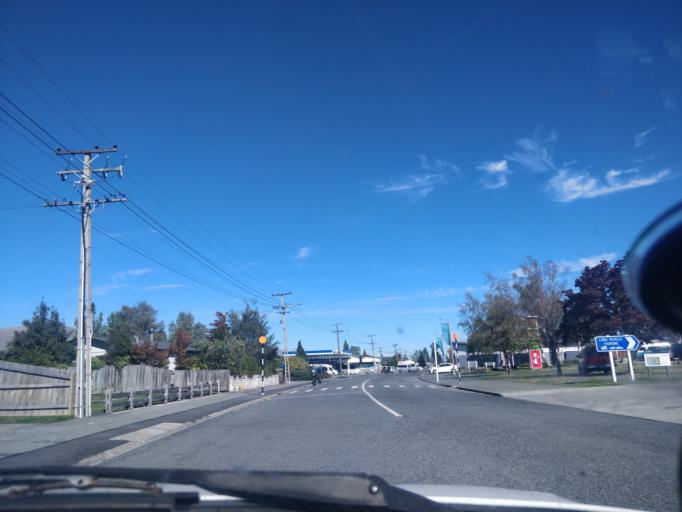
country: NZ
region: Canterbury
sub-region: Timaru District
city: Pleasant Point
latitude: -44.2567
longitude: 170.1008
